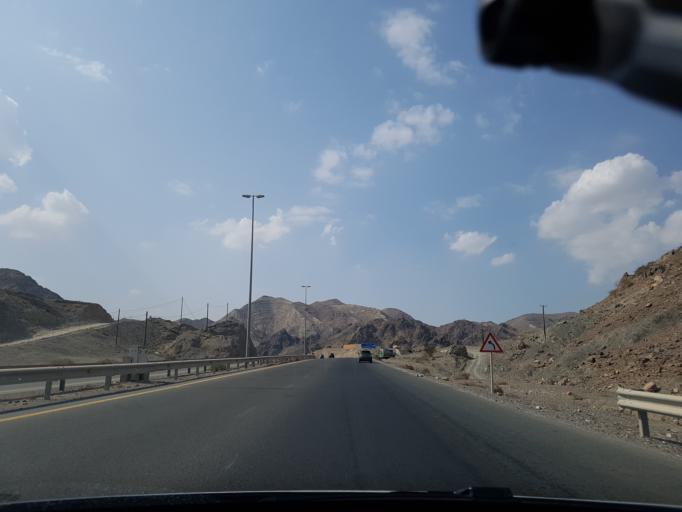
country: AE
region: Al Fujayrah
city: Dibba Al-Fujairah
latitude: 25.5320
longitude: 56.1357
